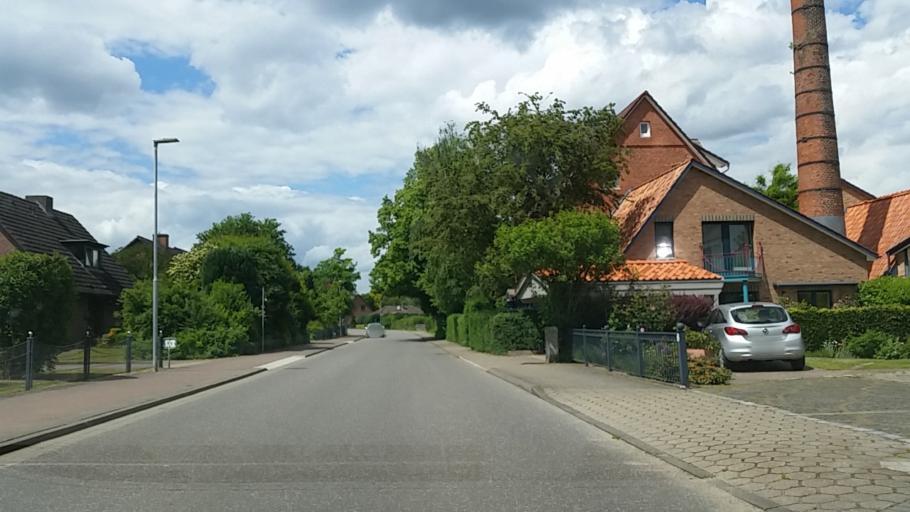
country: DE
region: Schleswig-Holstein
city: Dahmker
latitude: 53.5983
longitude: 10.4432
